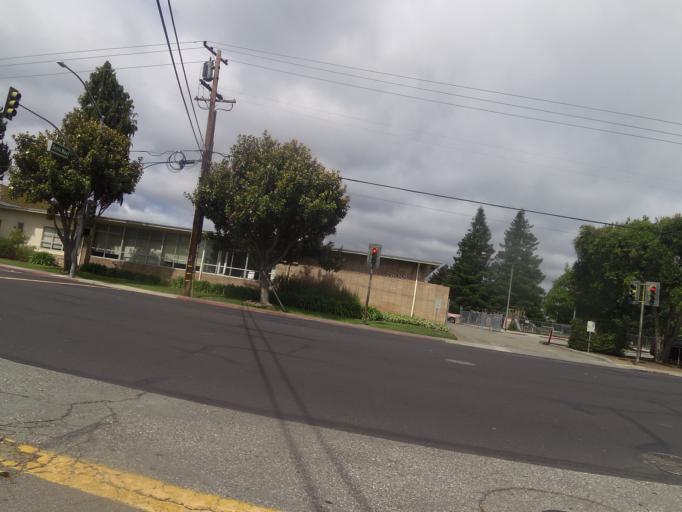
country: US
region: California
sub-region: Santa Clara County
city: Mountain View
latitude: 37.3849
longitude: -122.0869
